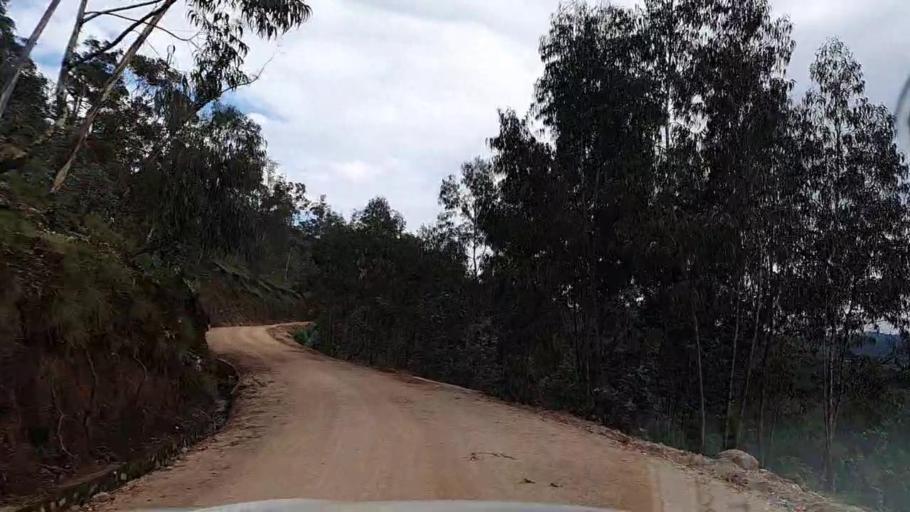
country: RW
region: Southern Province
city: Nzega
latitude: -2.3860
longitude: 29.4503
